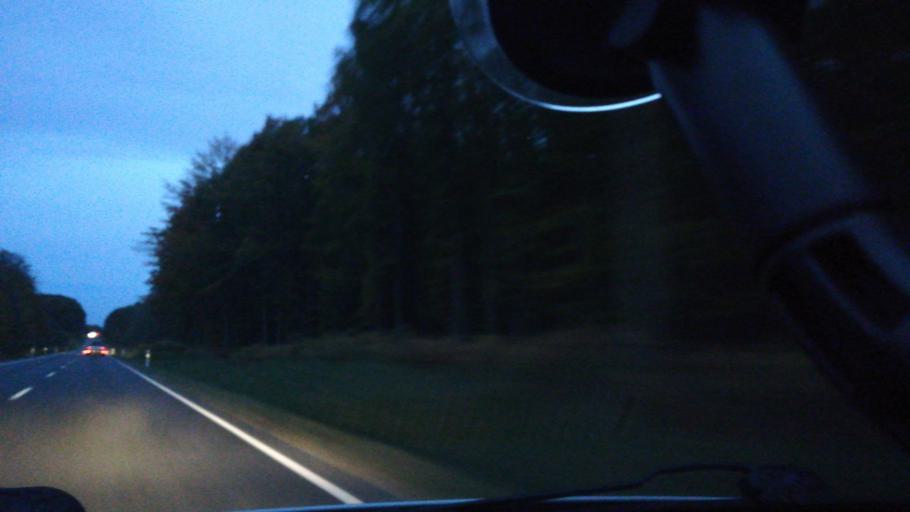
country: DE
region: Bavaria
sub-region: Regierungsbezirk Unterfranken
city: Bischbrunn
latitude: 49.8897
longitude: 9.4656
